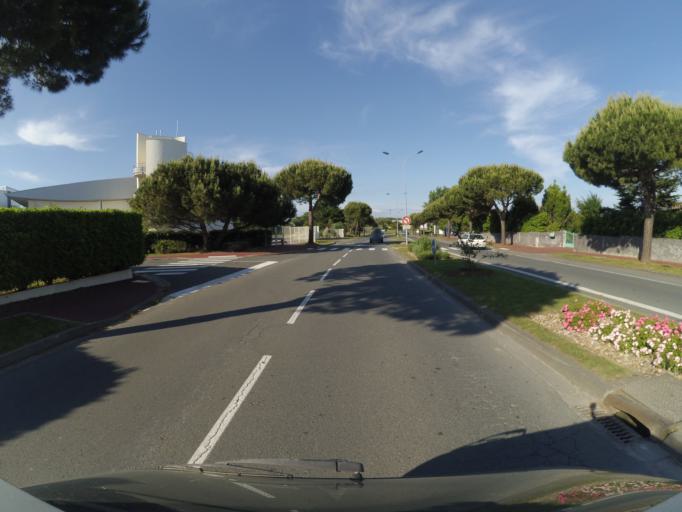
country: FR
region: Poitou-Charentes
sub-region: Departement de la Charente-Maritime
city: Royan
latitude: 45.6381
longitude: -1.0274
